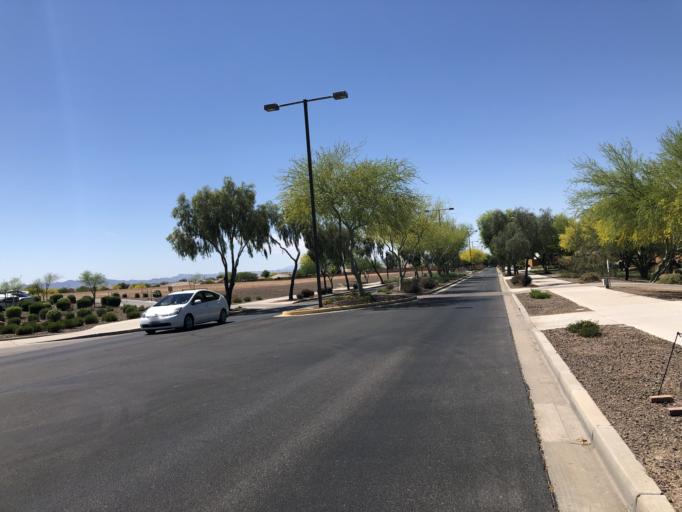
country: US
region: Arizona
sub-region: Maricopa County
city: Citrus Park
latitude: 33.6670
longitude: -112.6228
